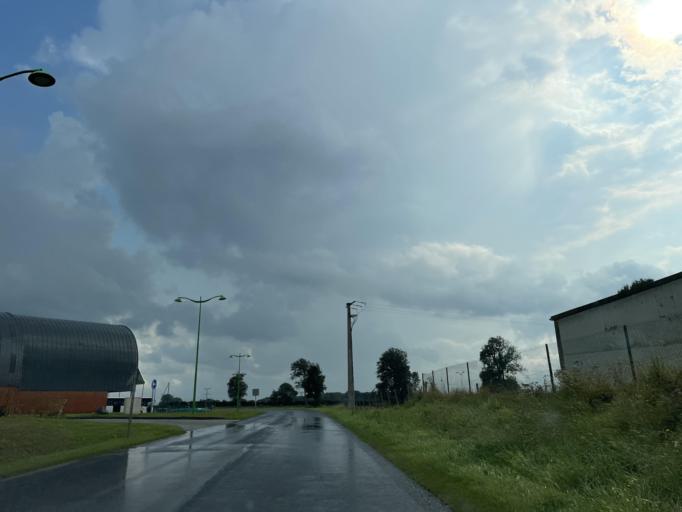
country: FR
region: Haute-Normandie
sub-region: Departement de la Seine-Maritime
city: Saint-Martin-en-Campagne
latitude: 49.9431
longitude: 1.2647
